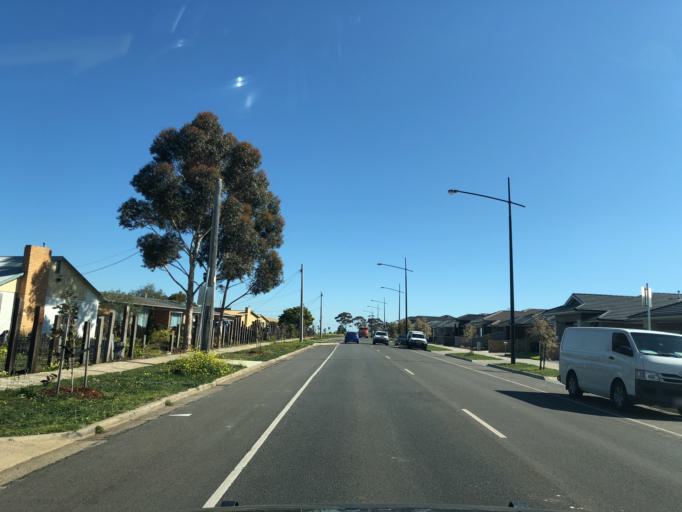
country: AU
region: Victoria
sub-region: Hume
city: Diggers Rest
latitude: -37.6281
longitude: 144.7153
